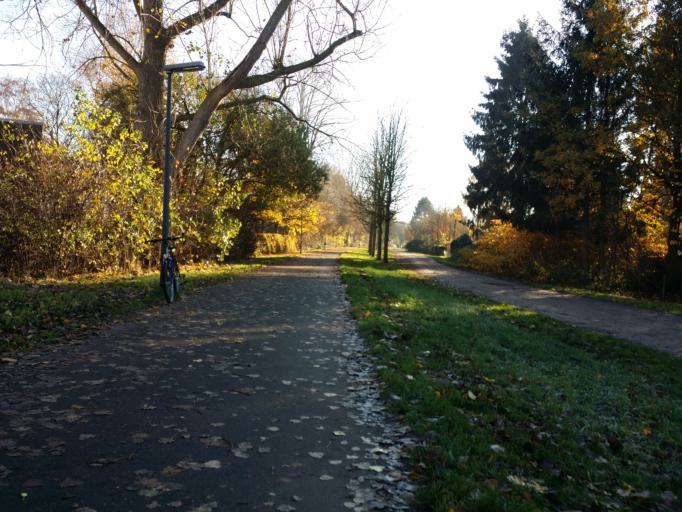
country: DE
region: Bremen
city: Bremen
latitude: 53.0724
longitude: 8.8736
